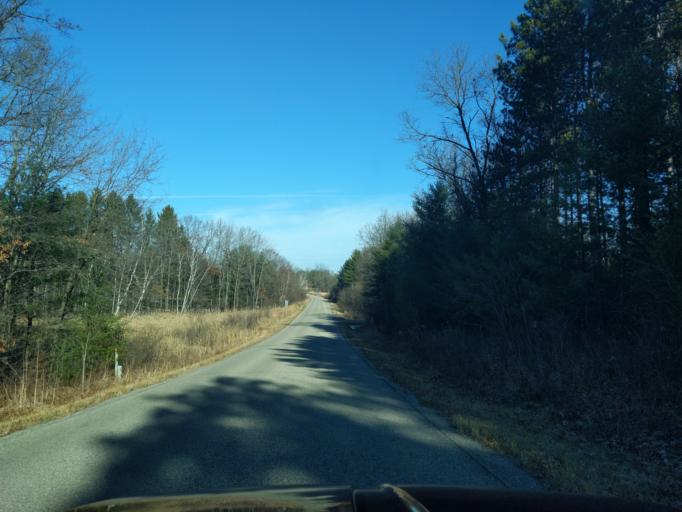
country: US
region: Wisconsin
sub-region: Waushara County
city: Silver Lake
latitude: 44.0596
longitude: -89.1887
